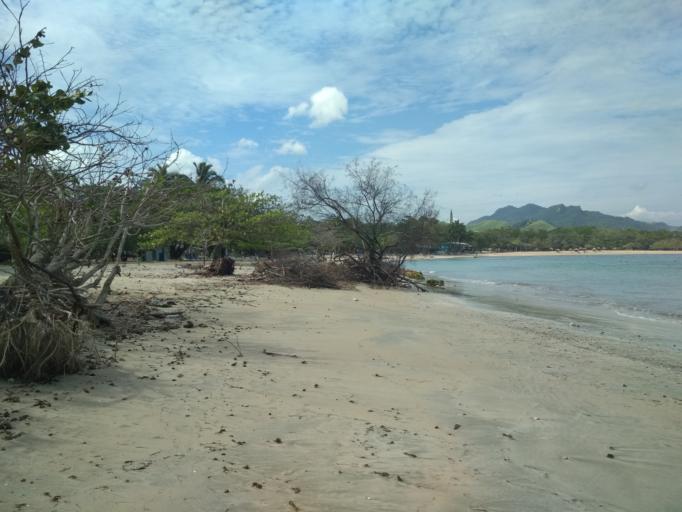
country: DO
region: Puerto Plata
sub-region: Puerto Plata
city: Puerto Plata
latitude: 19.8150
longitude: -70.7119
